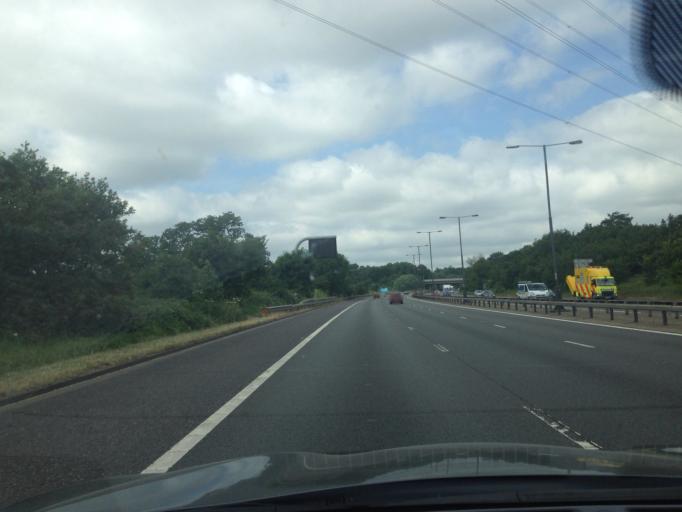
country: GB
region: England
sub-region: Hertfordshire
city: Elstree
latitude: 51.6354
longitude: -0.2923
